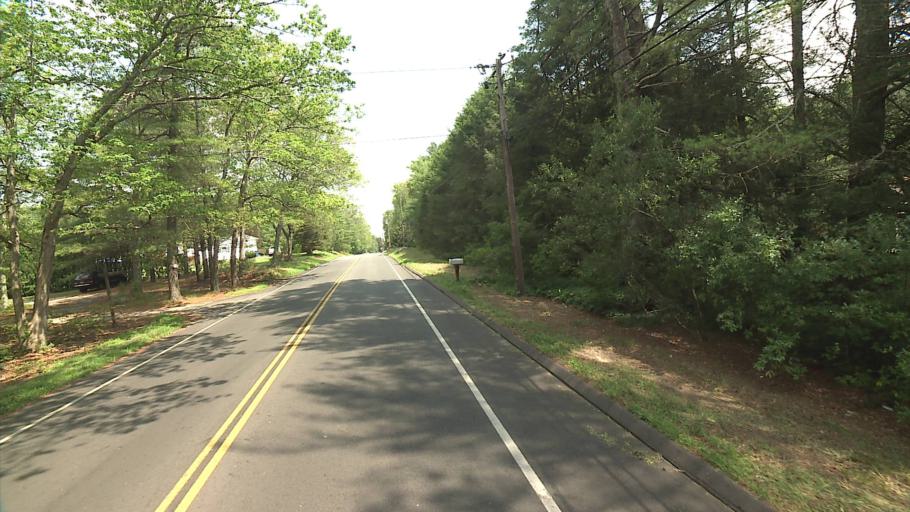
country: US
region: Connecticut
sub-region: New London County
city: Preston City
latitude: 41.5637
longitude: -71.8689
